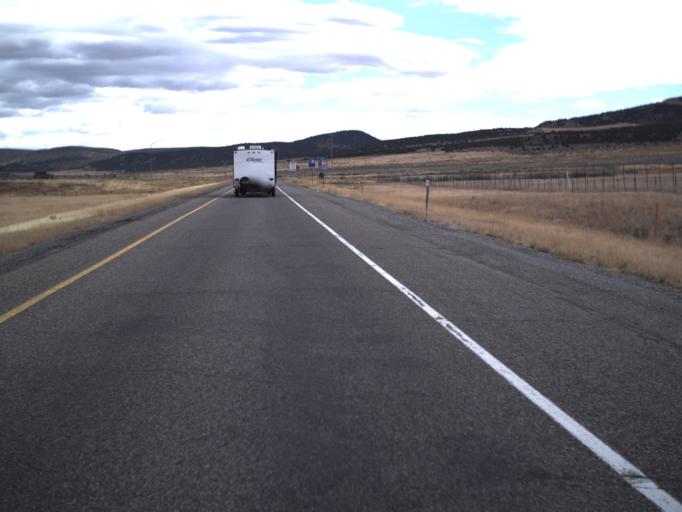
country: US
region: Idaho
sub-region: Oneida County
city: Malad City
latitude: 41.9605
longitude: -112.7141
